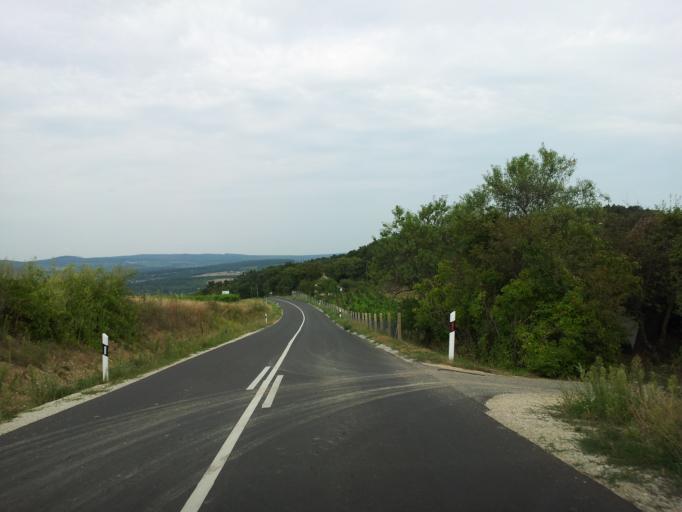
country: HU
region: Veszprem
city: Zanka
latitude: 46.9381
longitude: 17.7677
